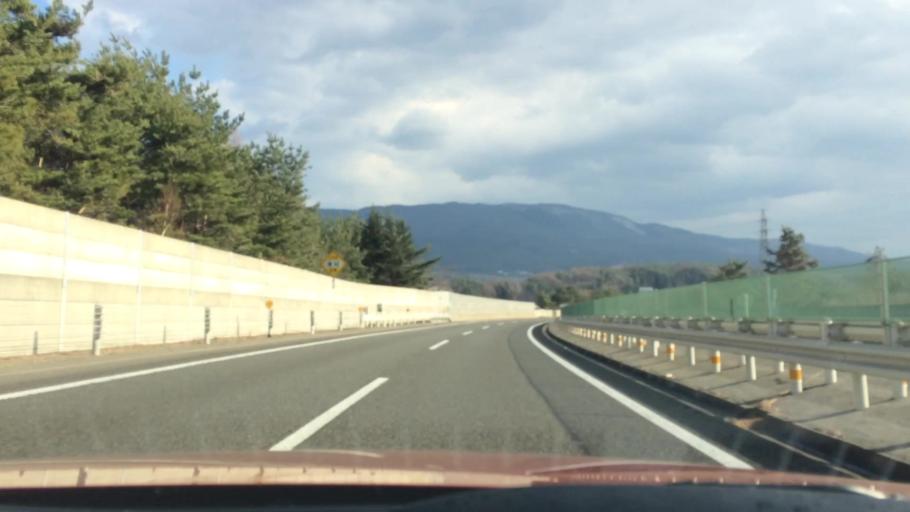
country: JP
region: Nagano
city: Shiojiri
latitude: 36.1656
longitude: 137.9632
